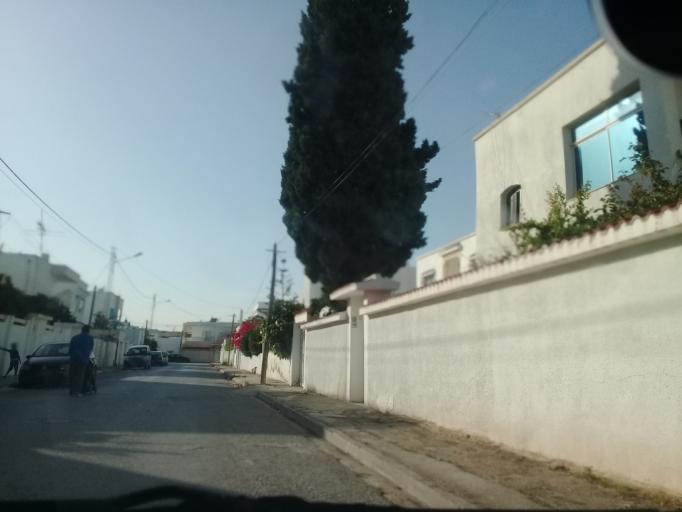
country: TN
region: Ariana
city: Ariana
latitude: 36.8343
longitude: 10.1967
